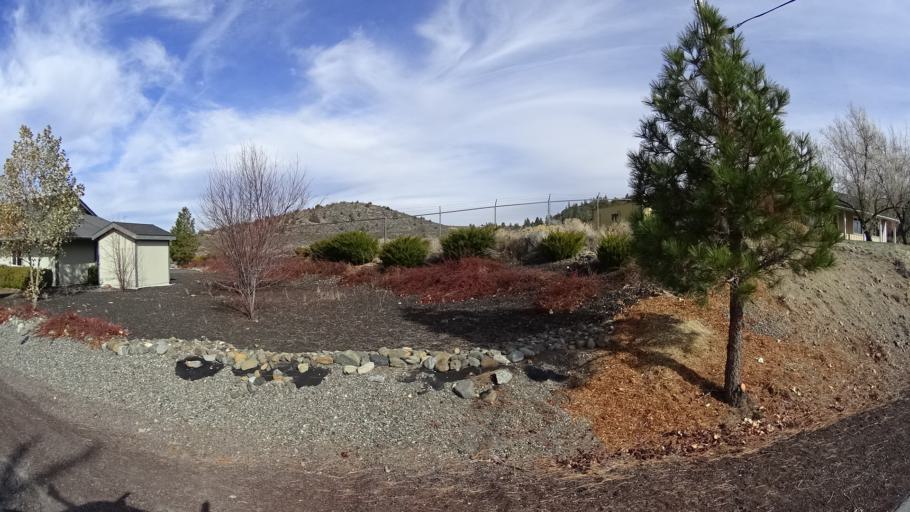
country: US
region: California
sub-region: Siskiyou County
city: Weed
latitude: 41.4745
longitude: -122.3544
